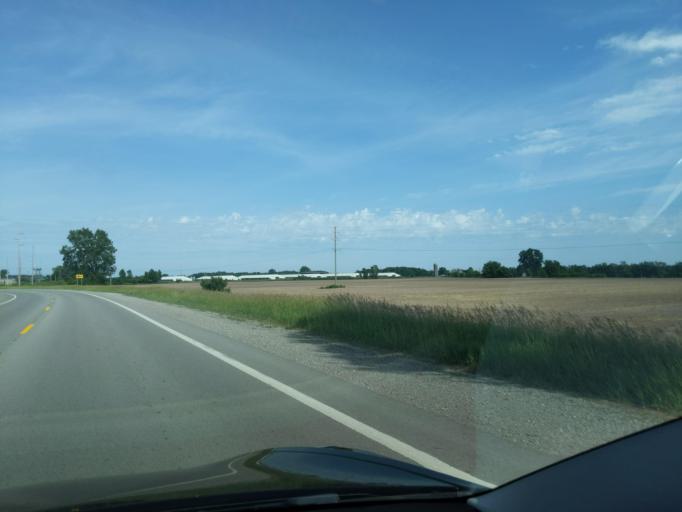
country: US
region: Michigan
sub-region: Newaygo County
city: Fremont
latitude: 43.4241
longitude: -86.0453
